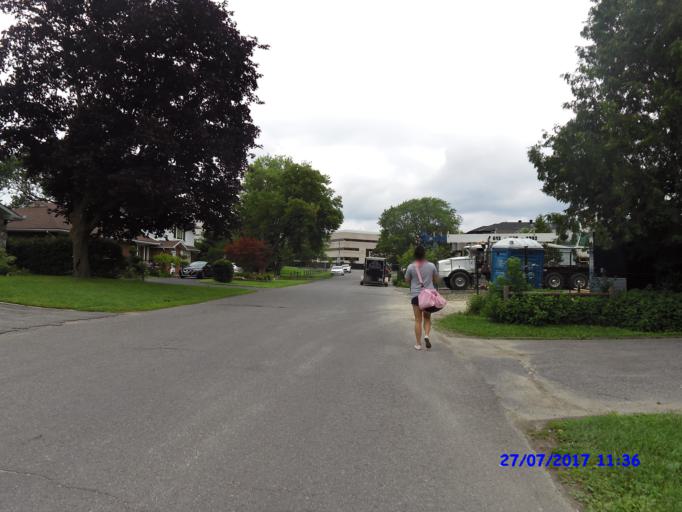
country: CA
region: Ontario
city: Ottawa
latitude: 45.3618
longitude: -75.7310
